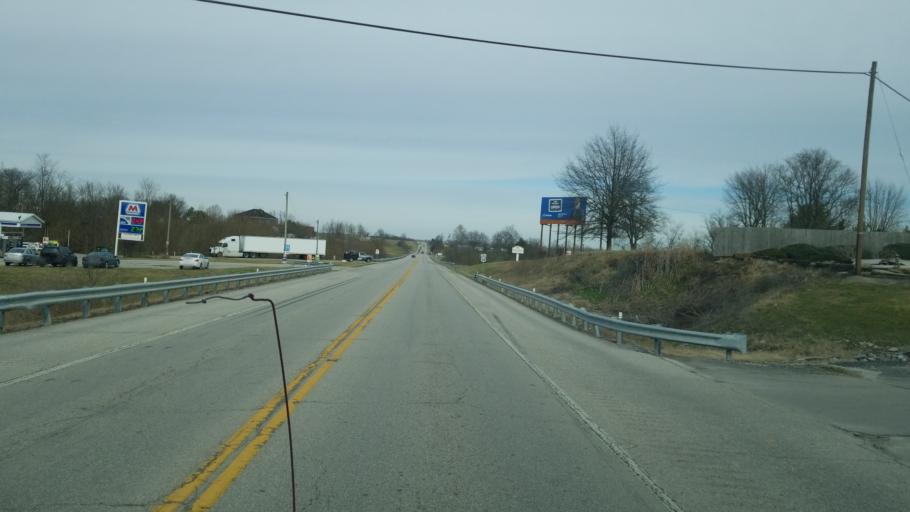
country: US
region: Kentucky
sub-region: Fleming County
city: Flemingsburg
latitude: 38.5180
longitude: -83.8377
